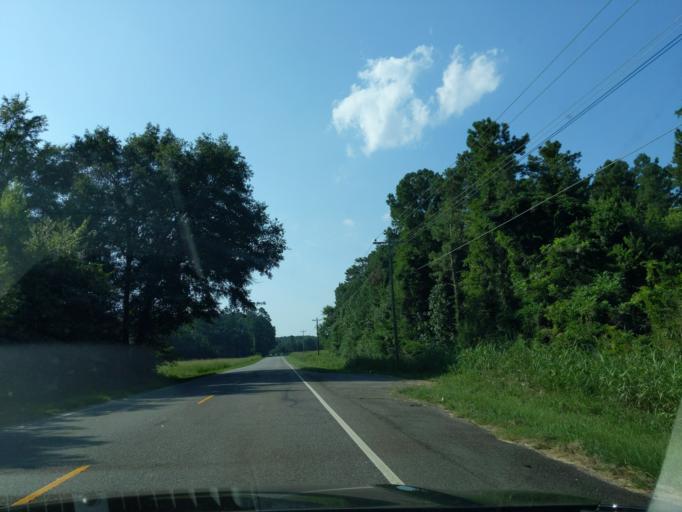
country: US
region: South Carolina
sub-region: Lexington County
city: Leesville
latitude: 34.0528
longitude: -81.5545
